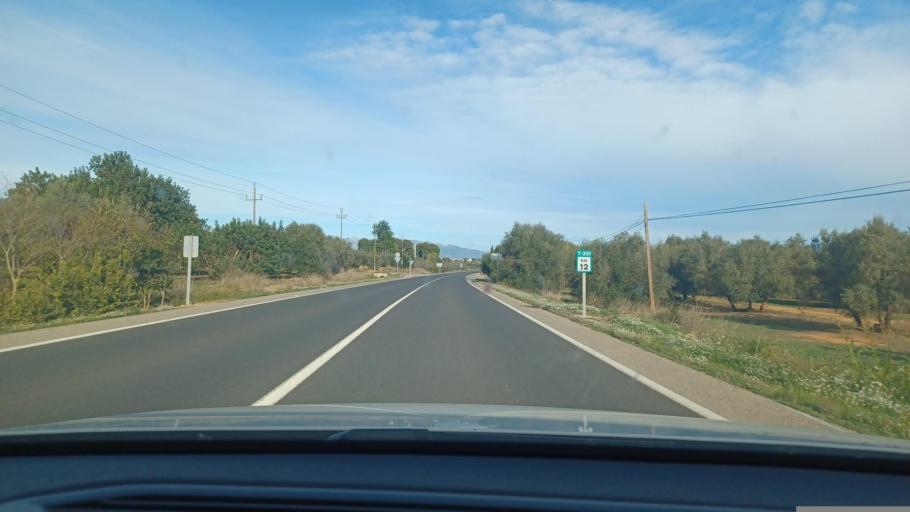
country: ES
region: Catalonia
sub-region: Provincia de Tarragona
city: Santa Barbara
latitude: 40.6893
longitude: 0.5072
